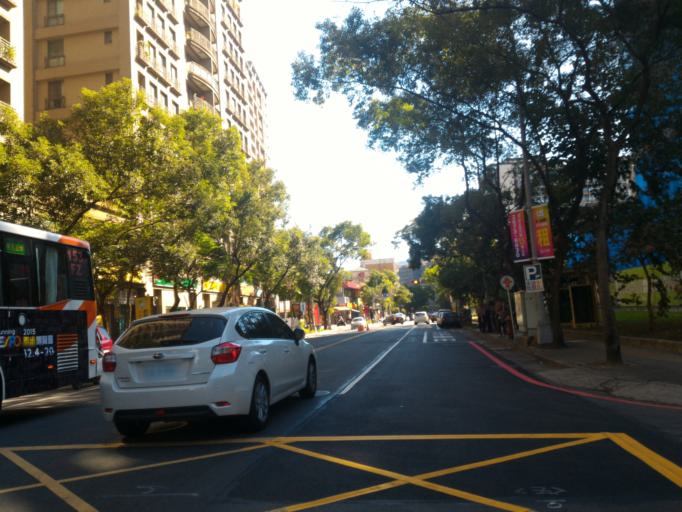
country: TW
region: Taiwan
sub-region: Taoyuan
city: Taoyuan
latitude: 24.9434
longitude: 121.3750
